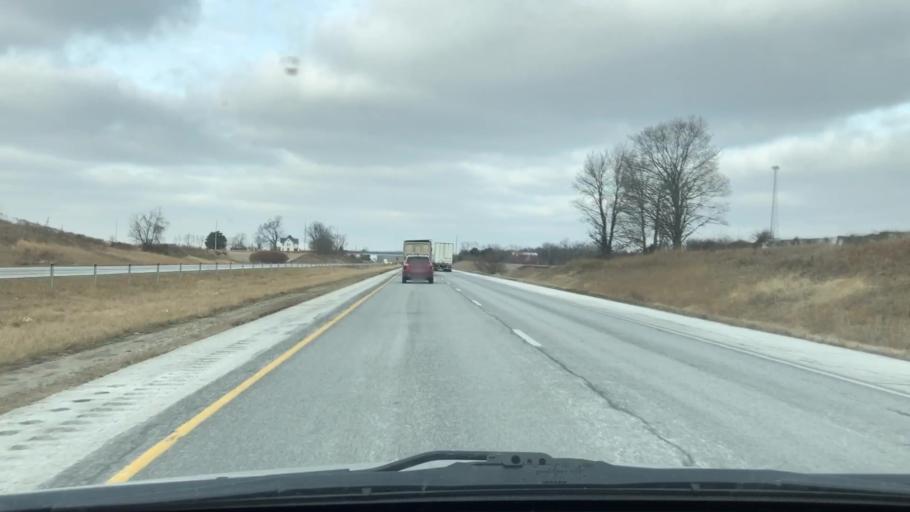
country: US
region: Indiana
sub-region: DeKalb County
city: Waterloo
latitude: 41.4864
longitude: -85.0540
